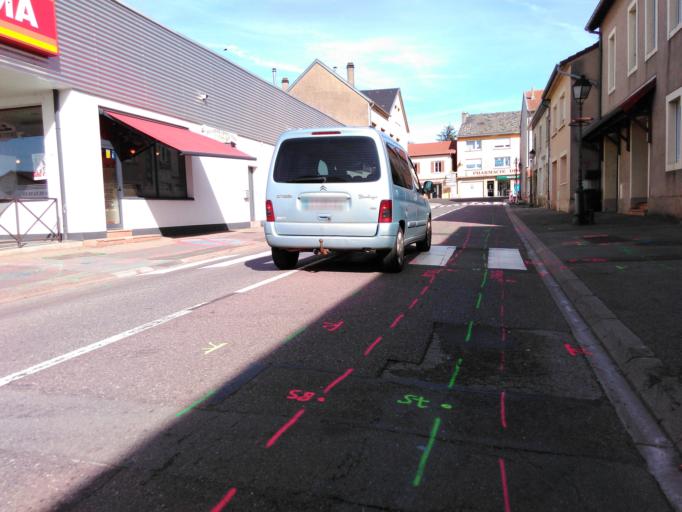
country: FR
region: Lorraine
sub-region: Departement de la Moselle
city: Hettange-Grande
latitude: 49.4055
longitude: 6.1547
